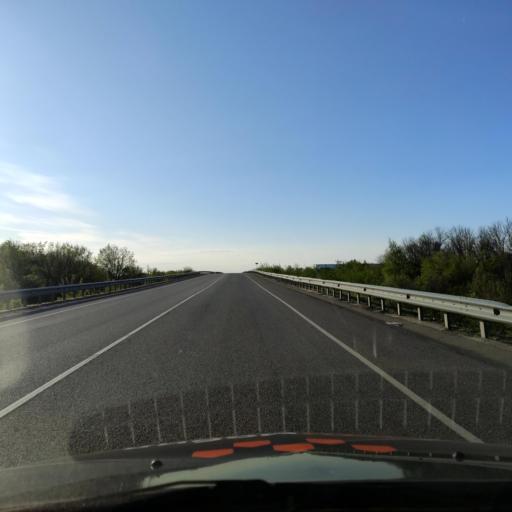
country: RU
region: Lipetsk
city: Yelets
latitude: 52.5657
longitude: 38.6736
